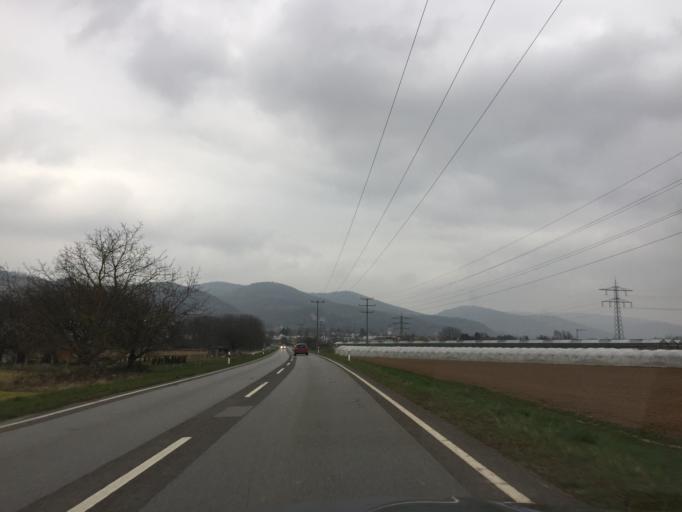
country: DE
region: Baden-Wuerttemberg
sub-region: Karlsruhe Region
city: Schriesheim
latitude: 49.4583
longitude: 8.6574
